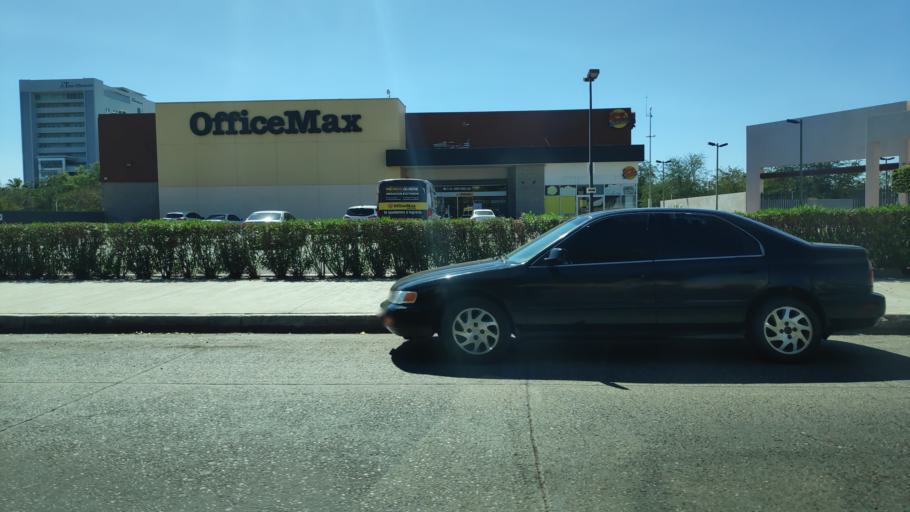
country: MX
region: Sinaloa
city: Culiacan
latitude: 24.8193
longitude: -107.4014
